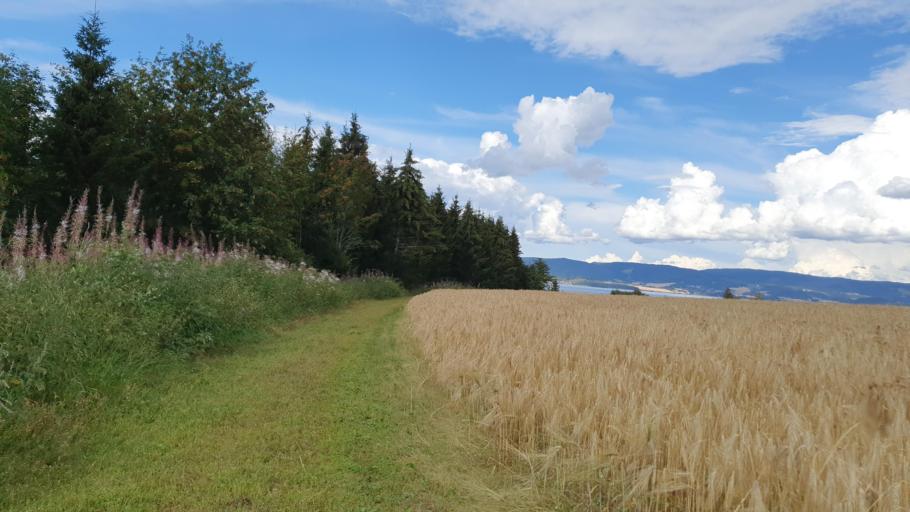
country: NO
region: Nord-Trondelag
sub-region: Levanger
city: Levanger
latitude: 63.7744
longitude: 11.3788
